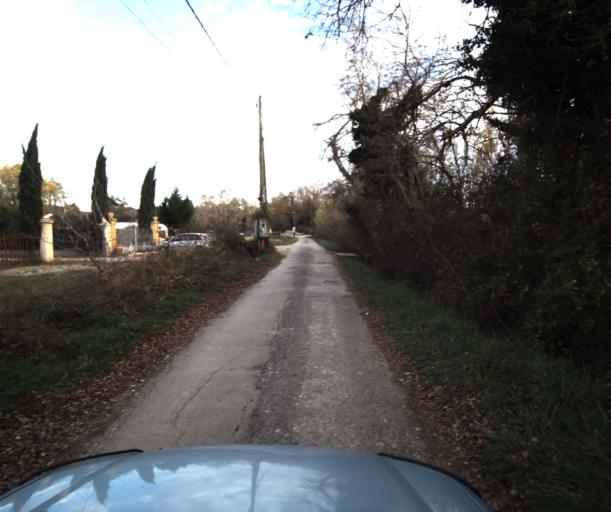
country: FR
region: Provence-Alpes-Cote d'Azur
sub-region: Departement des Bouches-du-Rhone
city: Meyrargues
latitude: 43.6662
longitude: 5.5266
